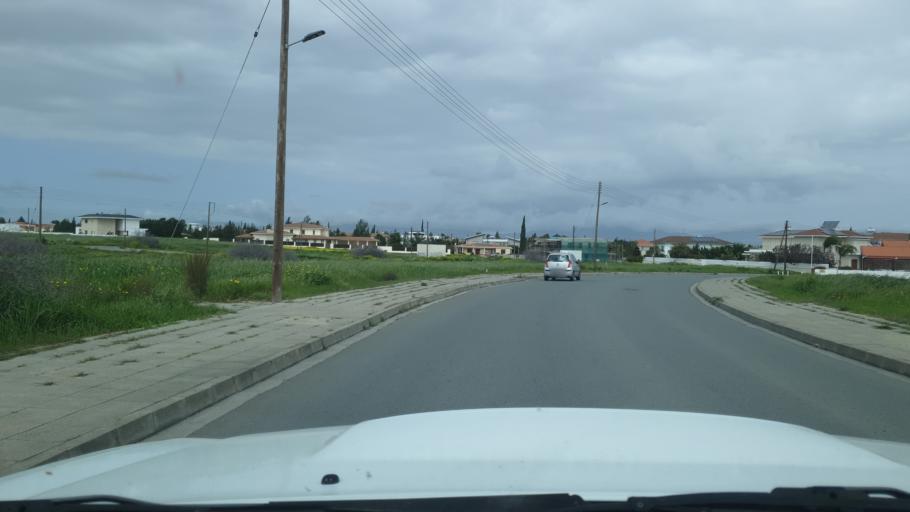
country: CY
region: Lefkosia
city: Tseri
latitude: 35.1022
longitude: 33.3548
